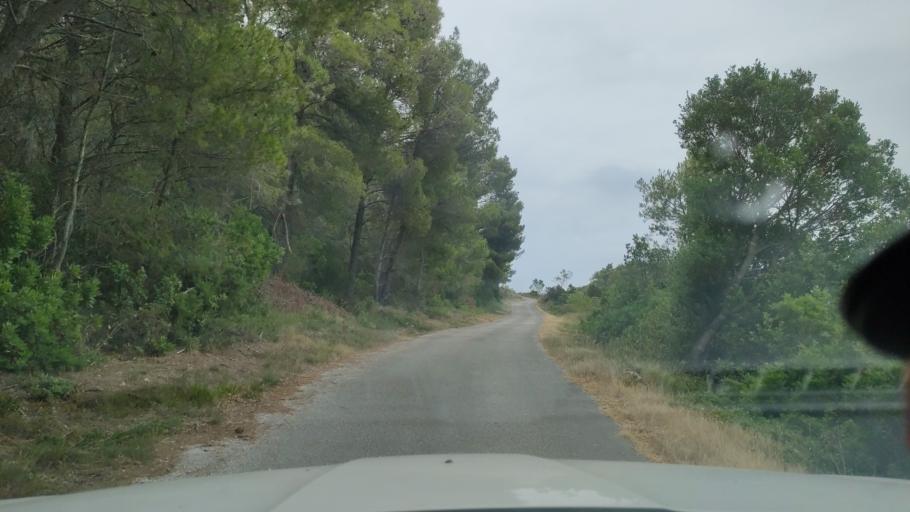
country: HR
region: Splitsko-Dalmatinska
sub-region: Grad Vis
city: Vis
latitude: 43.0302
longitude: 16.1679
